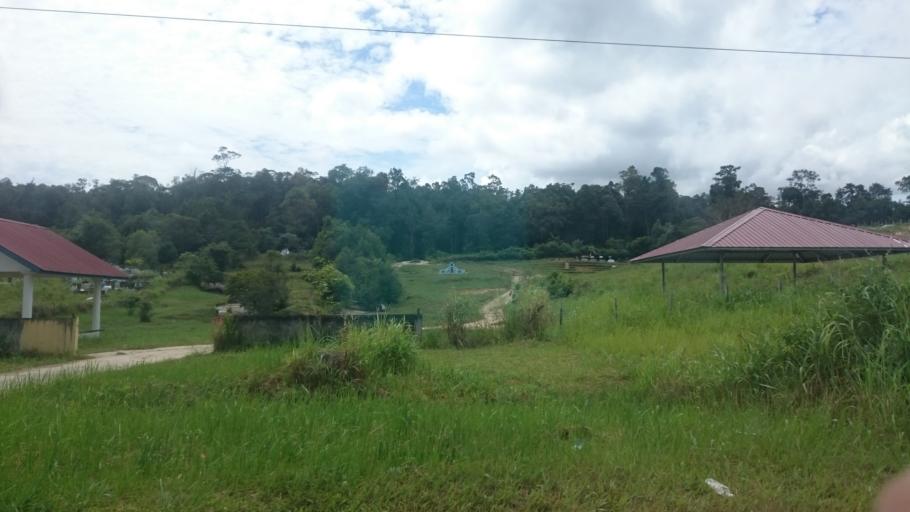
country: MY
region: Sarawak
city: Limbang
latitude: 4.6555
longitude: 114.9694
